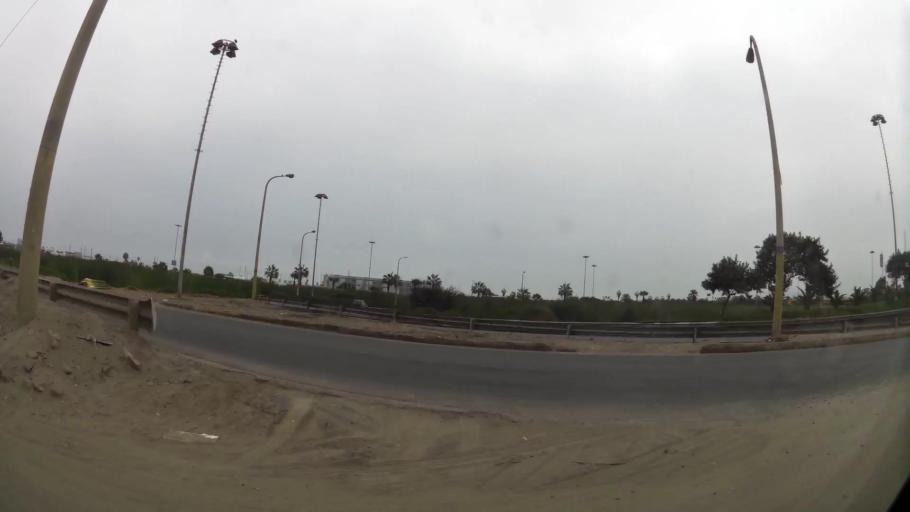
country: PE
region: Lima
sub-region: Lima
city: Surco
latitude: -12.2191
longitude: -76.9761
